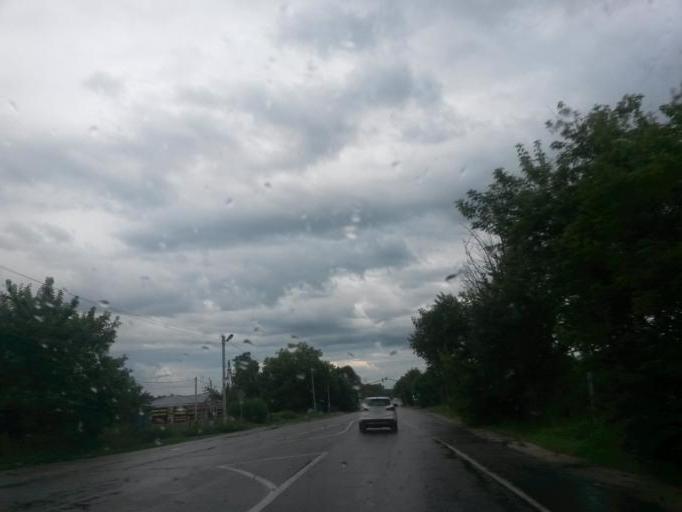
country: RU
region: Moskovskaya
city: Stolbovaya
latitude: 55.2687
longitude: 37.5112
